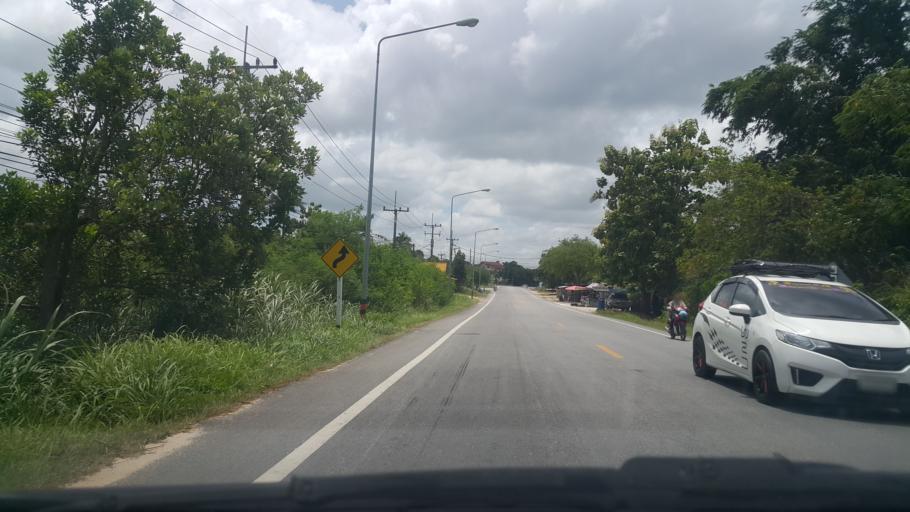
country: TH
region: Rayong
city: Ban Chang
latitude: 12.7890
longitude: 101.0297
